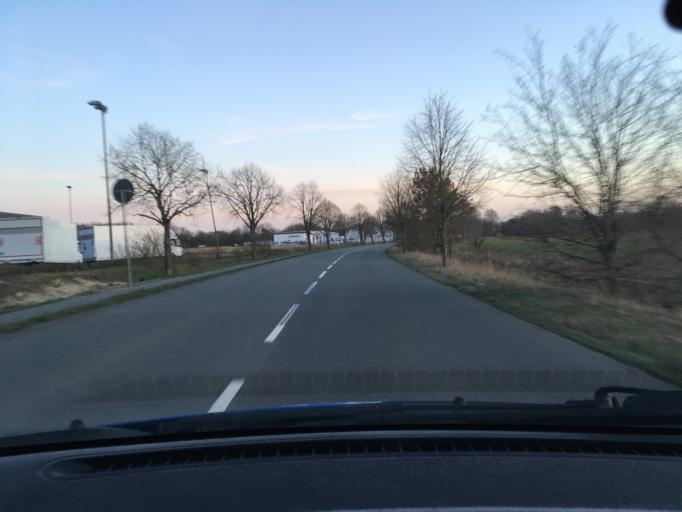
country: DE
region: Lower Saxony
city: Uelzen
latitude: 52.9840
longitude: 10.5713
